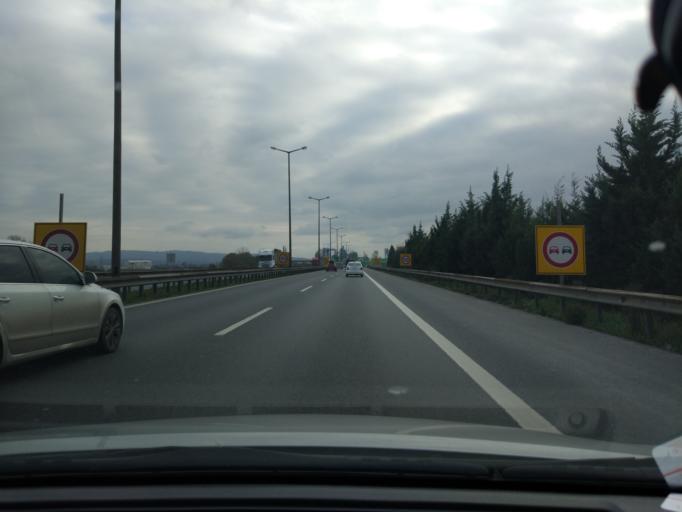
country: TR
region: Kocaeli
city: Kosekoy
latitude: 40.7671
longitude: 30.0188
